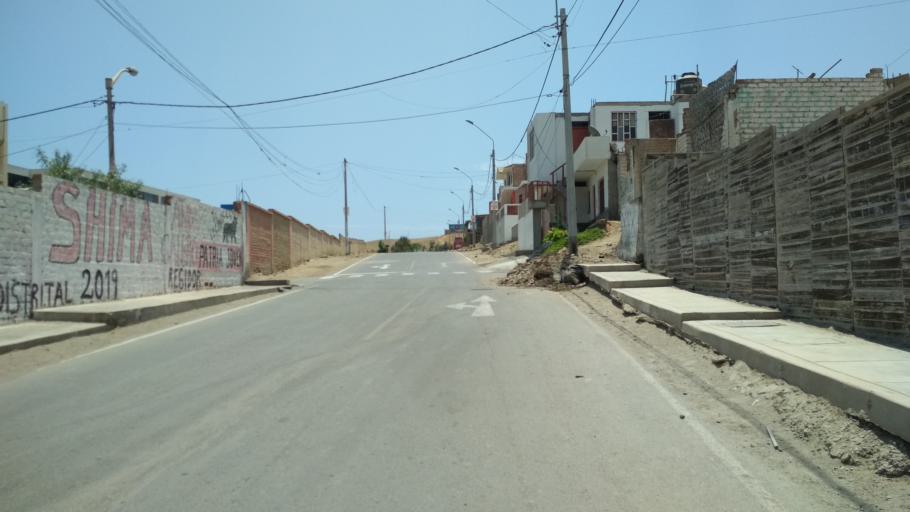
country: PE
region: Lima
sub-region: Barranca
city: Puerto Supe
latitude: -10.8050
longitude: -77.7441
